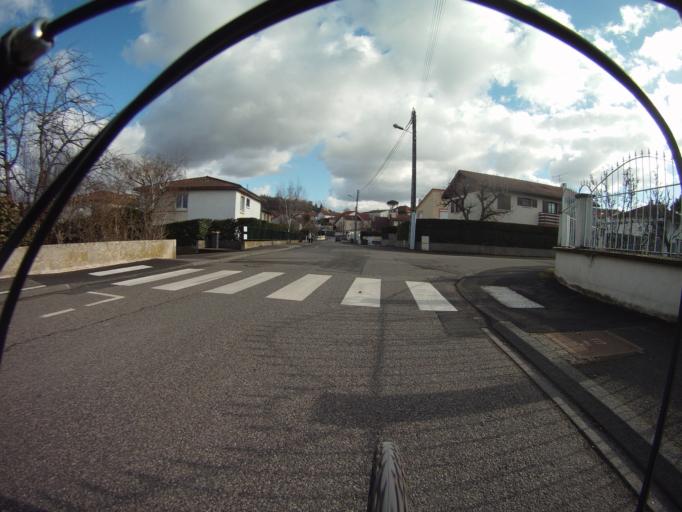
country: FR
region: Auvergne
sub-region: Departement du Puy-de-Dome
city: Aubiere
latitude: 45.7443
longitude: 3.1065
